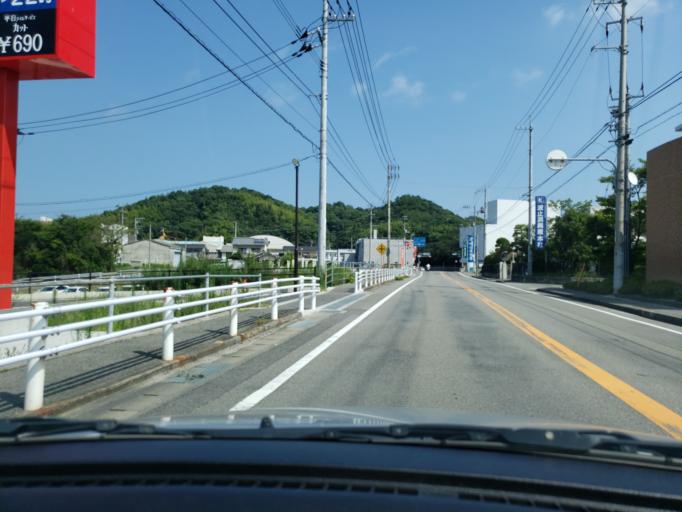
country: JP
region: Ehime
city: Hojo
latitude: 34.1039
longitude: 132.9671
